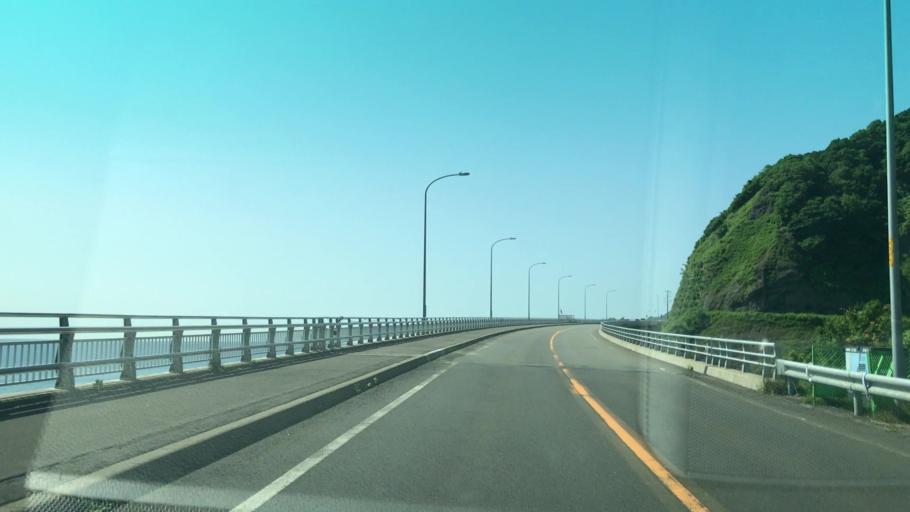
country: JP
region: Hokkaido
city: Iwanai
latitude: 43.1297
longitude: 140.4377
